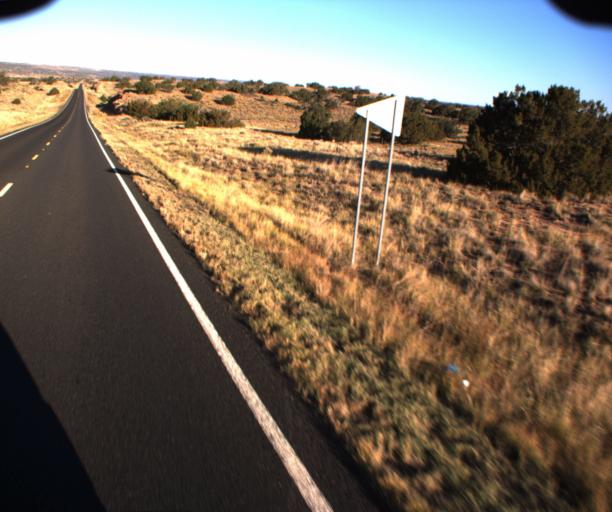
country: US
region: Arizona
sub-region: Apache County
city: Houck
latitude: 35.3654
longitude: -109.4725
